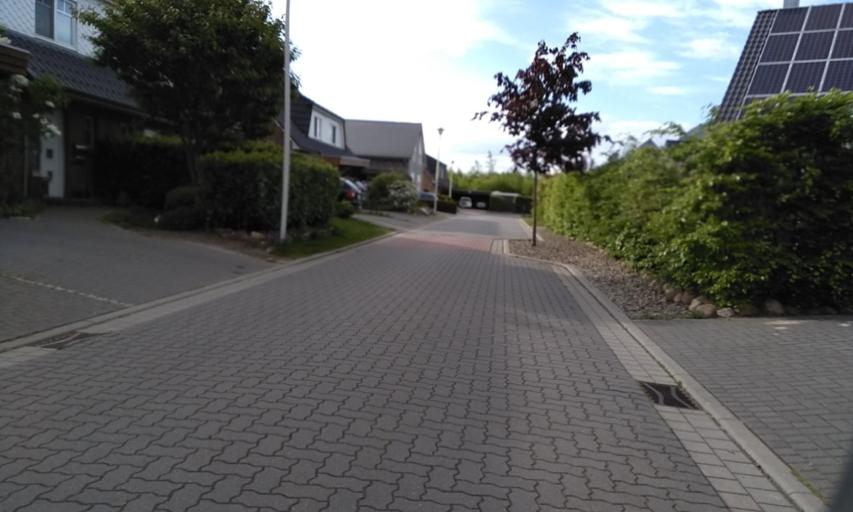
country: DE
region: Lower Saxony
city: Apensen
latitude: 53.4434
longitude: 9.6271
